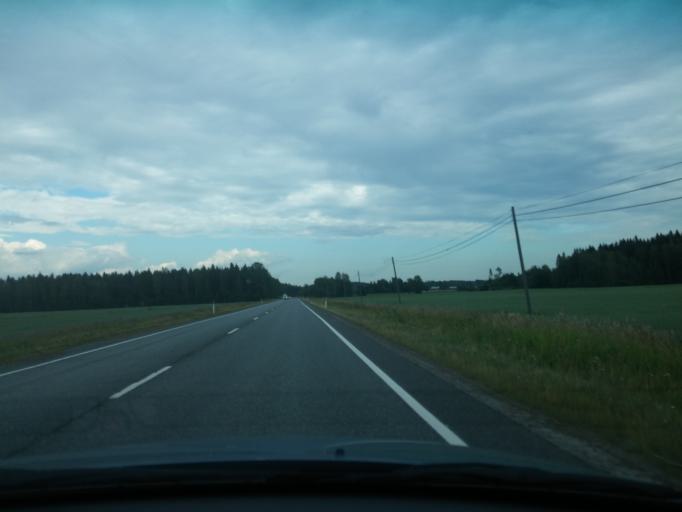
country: FI
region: Haeme
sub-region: Haemeenlinna
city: Tervakoski
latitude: 60.7399
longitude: 24.6124
